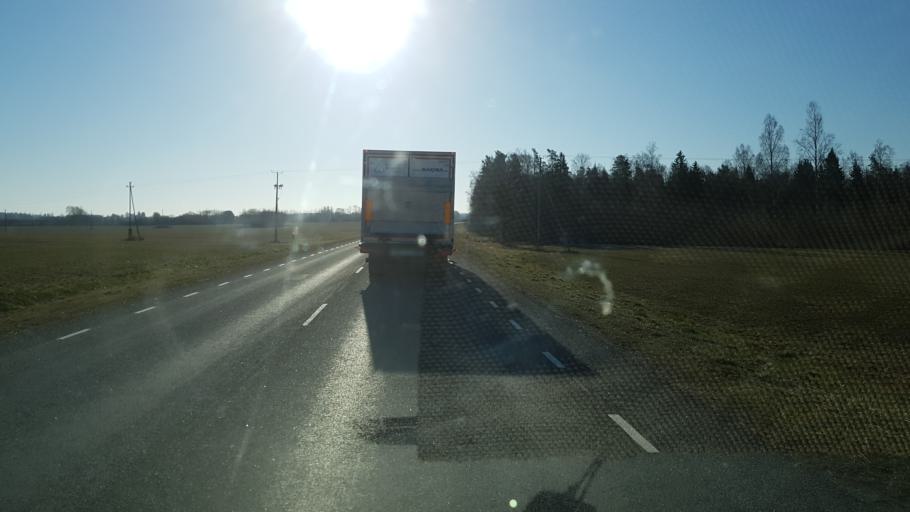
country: EE
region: Jaervamaa
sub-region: Tueri vald
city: Sarevere
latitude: 58.7787
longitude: 25.4935
